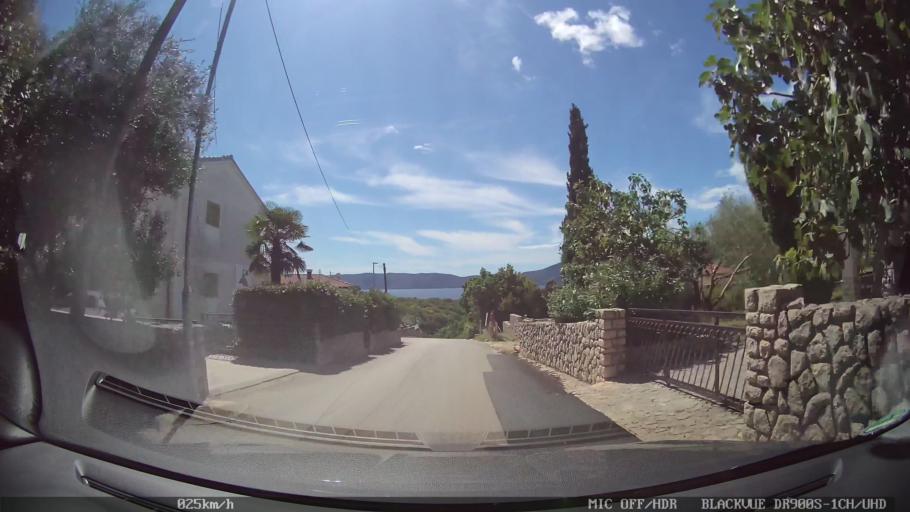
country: HR
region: Primorsko-Goranska
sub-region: Grad Krk
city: Krk
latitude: 45.0422
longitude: 14.4817
